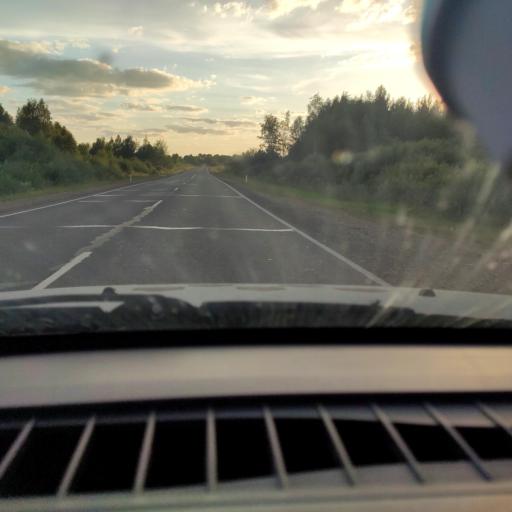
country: RU
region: Kirov
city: Kotel'nich
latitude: 58.3366
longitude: 48.3224
